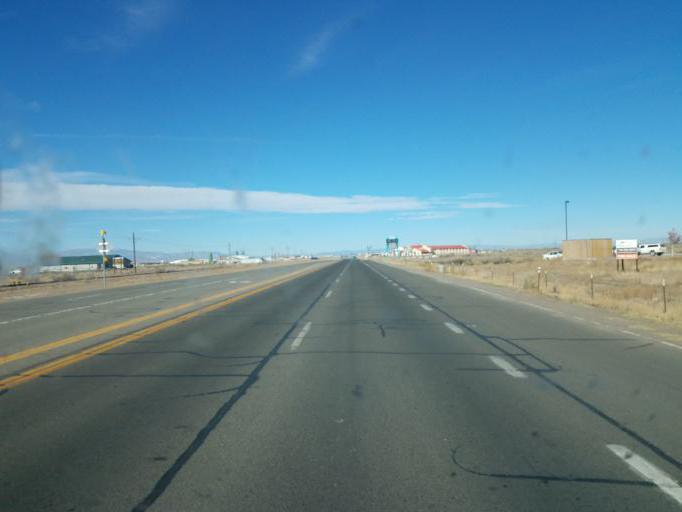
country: US
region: Colorado
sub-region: Alamosa County
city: Alamosa
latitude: 37.4809
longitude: -105.9078
